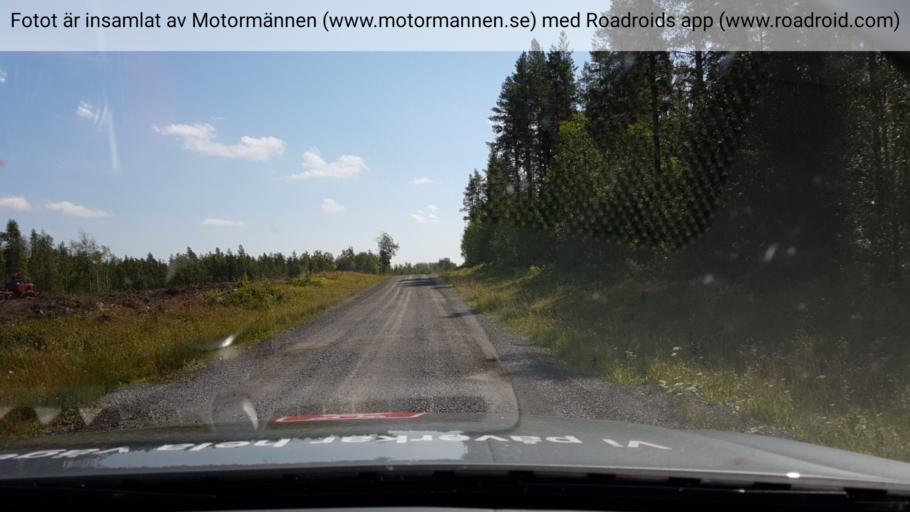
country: SE
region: Jaemtland
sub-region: OEstersunds Kommun
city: Lit
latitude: 63.3546
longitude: 15.3302
